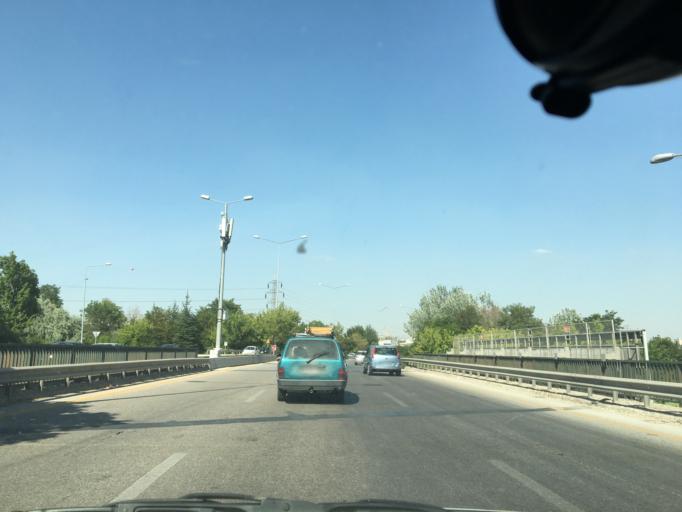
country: TR
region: Ankara
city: Batikent
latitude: 39.9180
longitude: 32.7800
